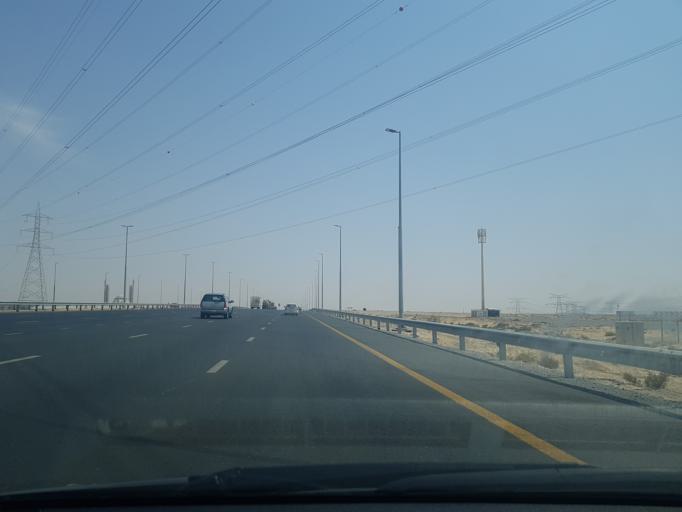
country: AE
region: Ash Shariqah
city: Sharjah
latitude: 25.2422
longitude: 55.5556
